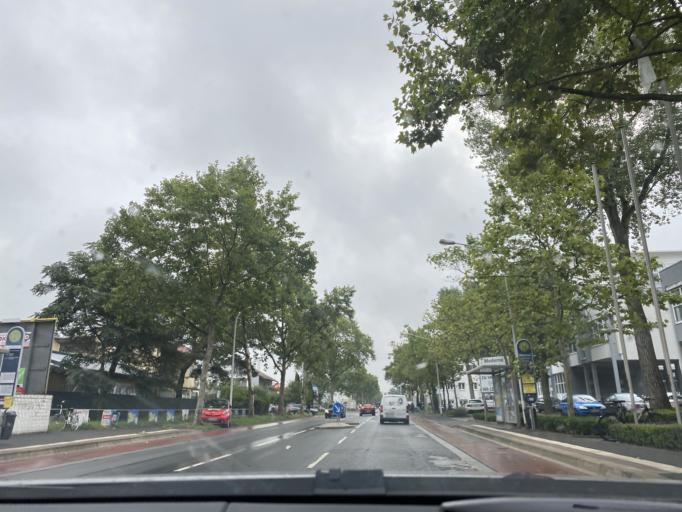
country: DE
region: Hesse
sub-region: Regierungsbezirk Darmstadt
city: Darmstadt
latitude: 49.8844
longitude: 8.6312
